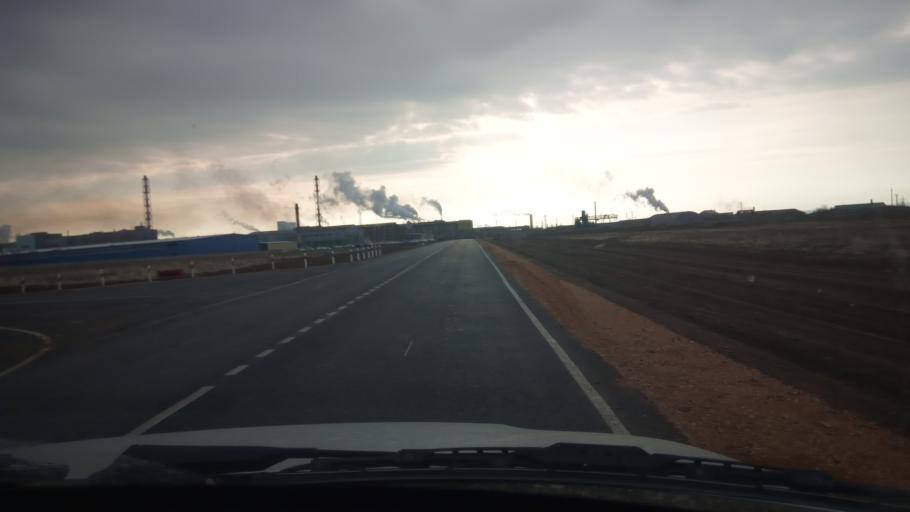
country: RU
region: Orenburg
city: Novotroitsk
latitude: 51.2407
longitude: 58.3265
